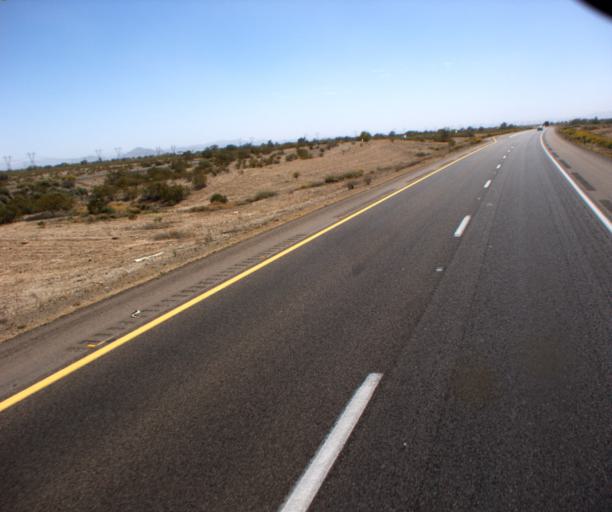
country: US
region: Arizona
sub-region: Maricopa County
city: Gila Bend
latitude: 33.0468
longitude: -112.6445
